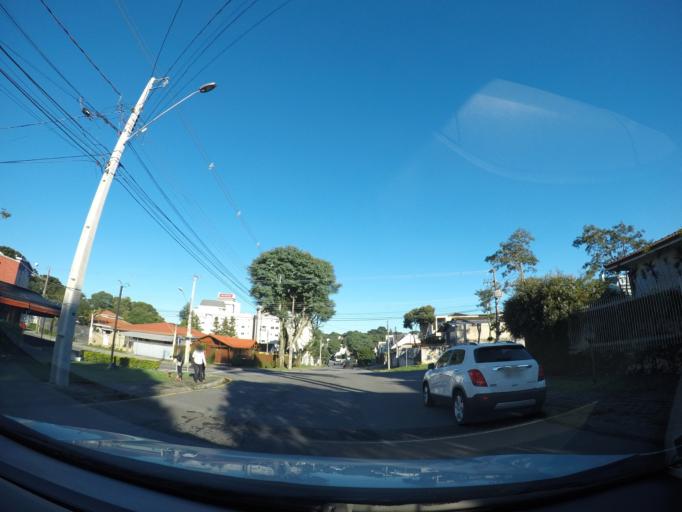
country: BR
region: Parana
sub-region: Curitiba
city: Curitiba
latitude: -25.4071
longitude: -49.2684
